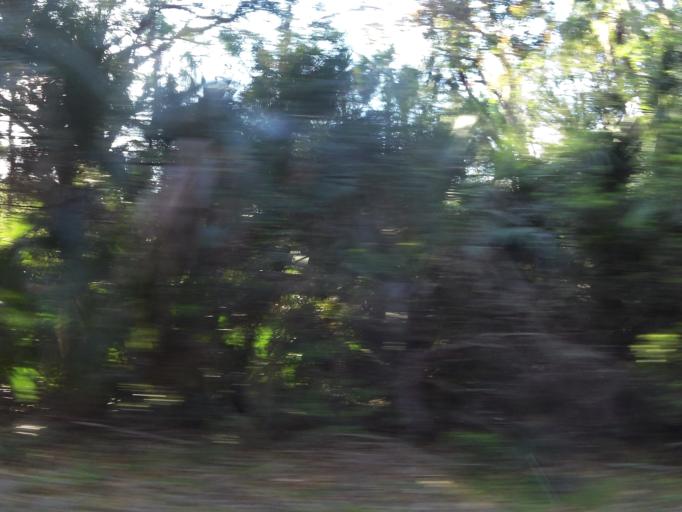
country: US
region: Florida
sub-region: Duval County
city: Atlantic Beach
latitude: 30.3686
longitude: -81.4006
